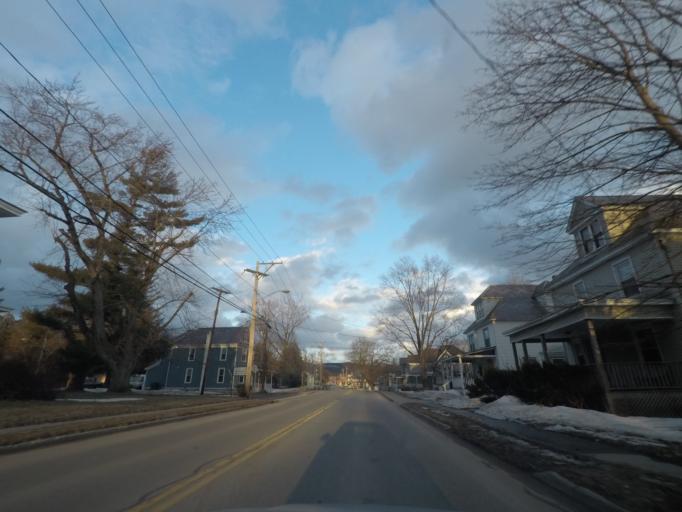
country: US
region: New York
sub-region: Montgomery County
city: Saint Johnsville
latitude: 42.9984
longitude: -74.6869
